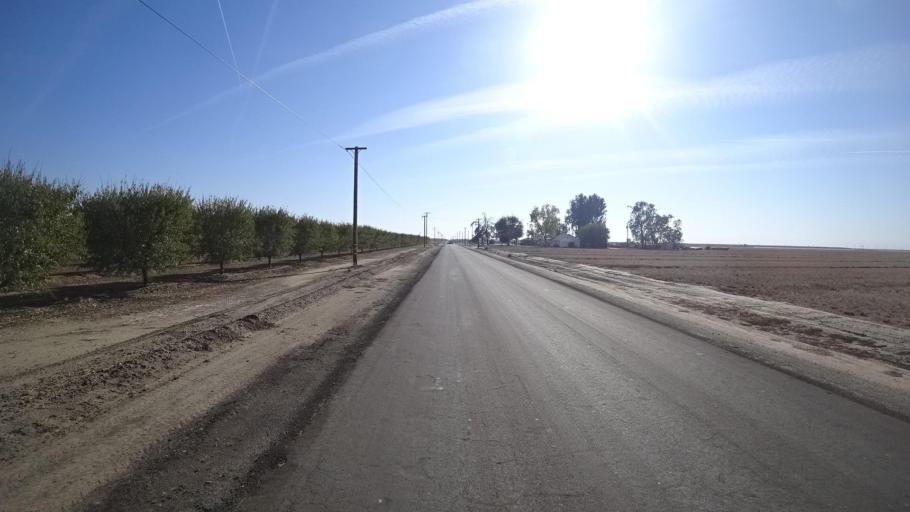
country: US
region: California
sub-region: Kern County
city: Wasco
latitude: 35.6689
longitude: -119.3840
